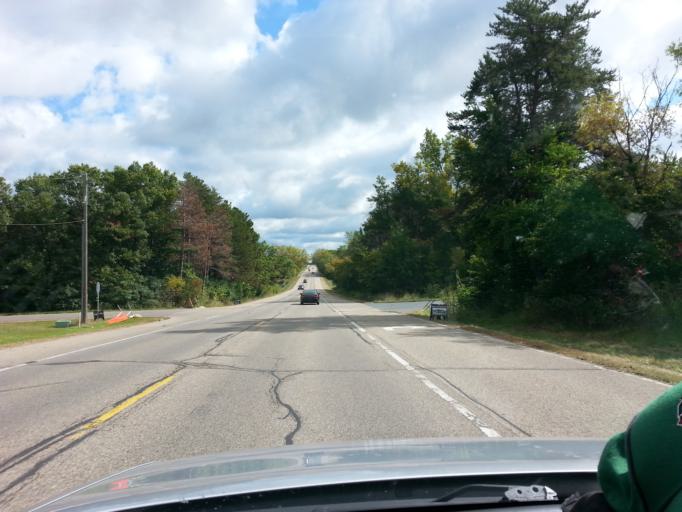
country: US
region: Minnesota
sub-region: Washington County
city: Lake Elmo
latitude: 44.9635
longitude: -92.9142
